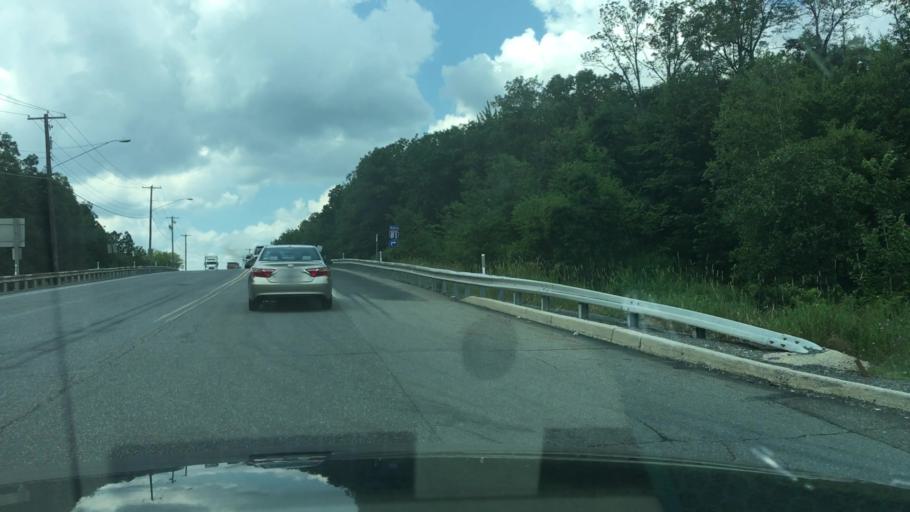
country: US
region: Pennsylvania
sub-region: Schuylkill County
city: Ashland
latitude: 40.7144
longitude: -76.3415
